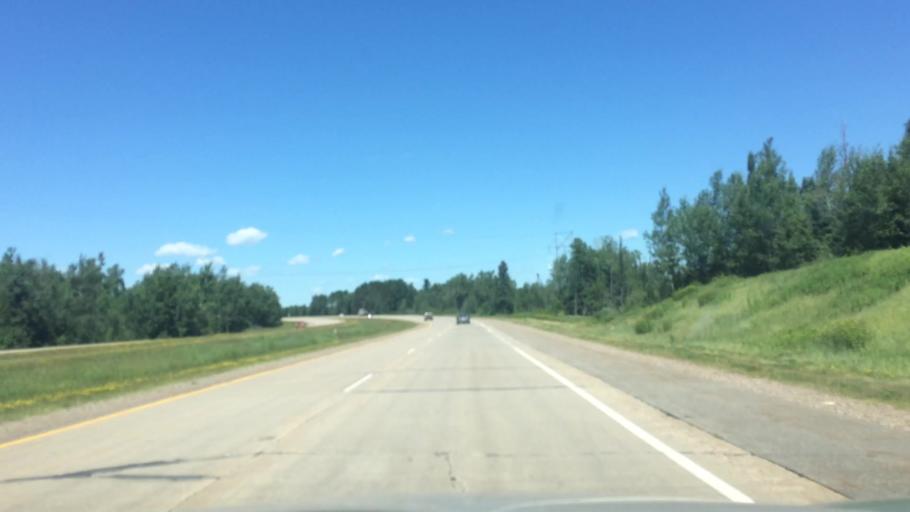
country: US
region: Wisconsin
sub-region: Lincoln County
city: Tomahawk
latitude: 45.3719
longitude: -89.6668
